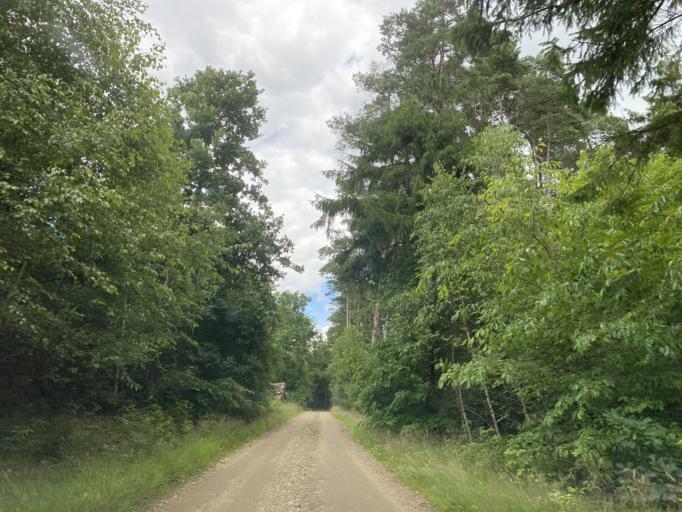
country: DK
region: Central Jutland
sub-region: Viborg Kommune
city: Bjerringbro
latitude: 56.2855
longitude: 9.6549
